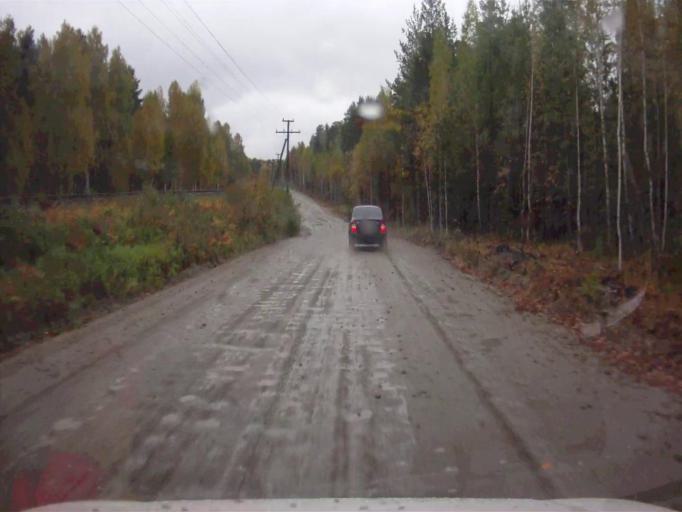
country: RU
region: Chelyabinsk
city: Kyshtym
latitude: 55.7962
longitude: 60.4817
